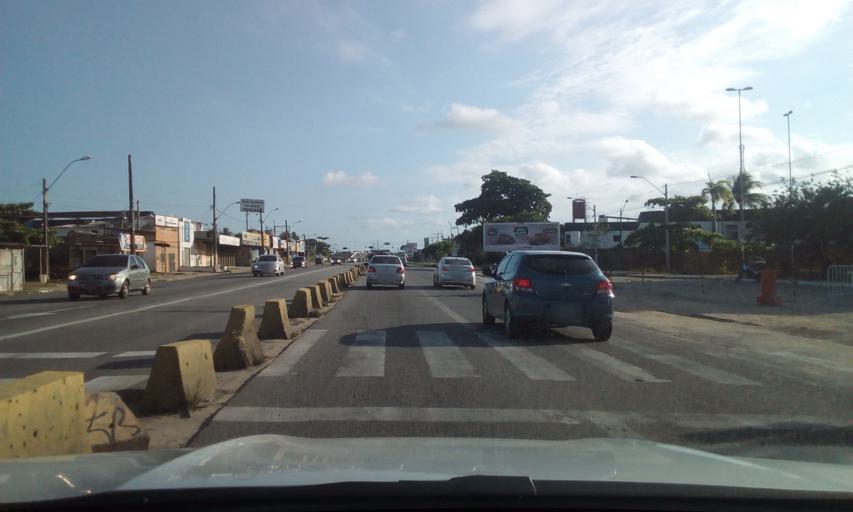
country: BR
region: Pernambuco
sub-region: Olinda
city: Olinda
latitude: -8.0122
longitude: -34.8592
